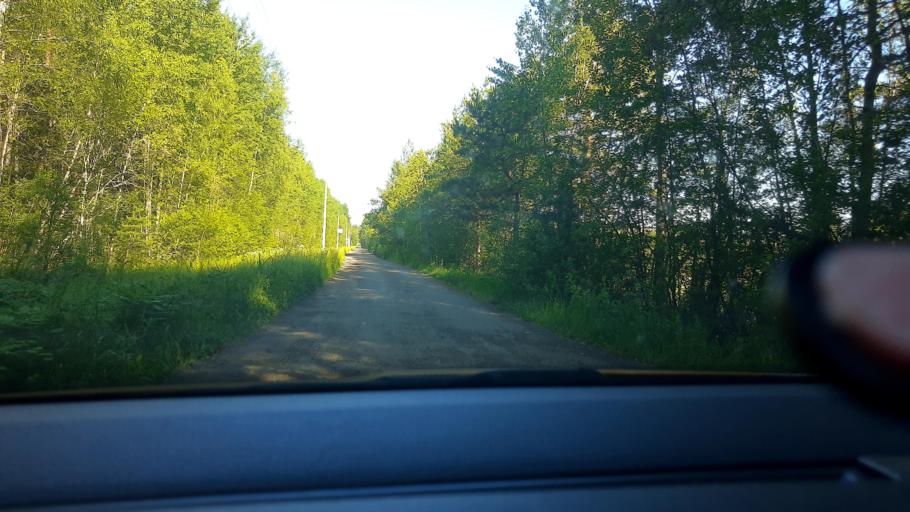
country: RU
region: Moskovskaya
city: Elektrogorsk
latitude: 55.8978
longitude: 38.7116
